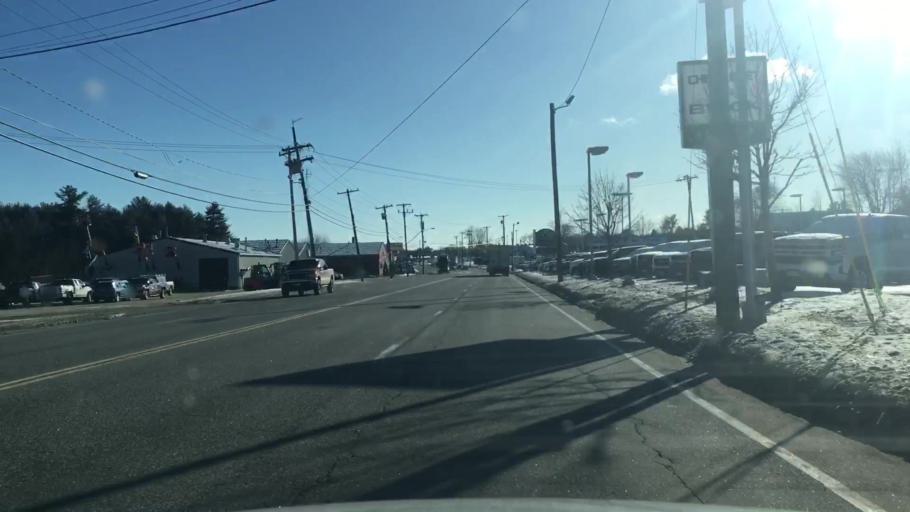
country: US
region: Maine
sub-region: Androscoggin County
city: Lewiston
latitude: 44.1342
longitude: -70.2256
